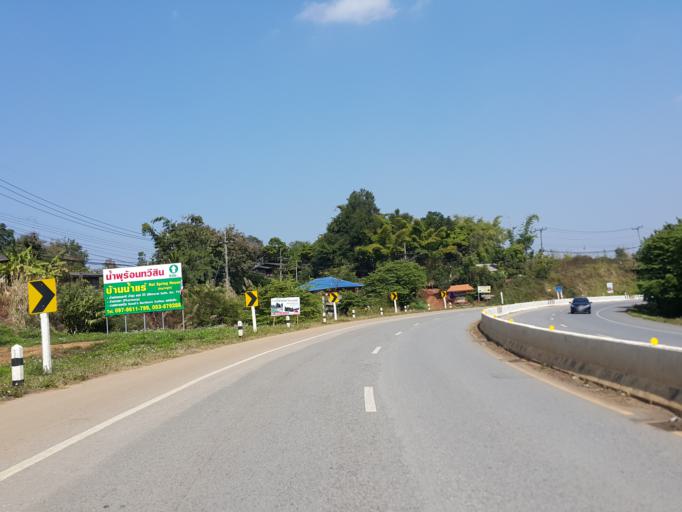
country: TH
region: Lampang
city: Wang Nuea
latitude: 19.1118
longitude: 99.4573
